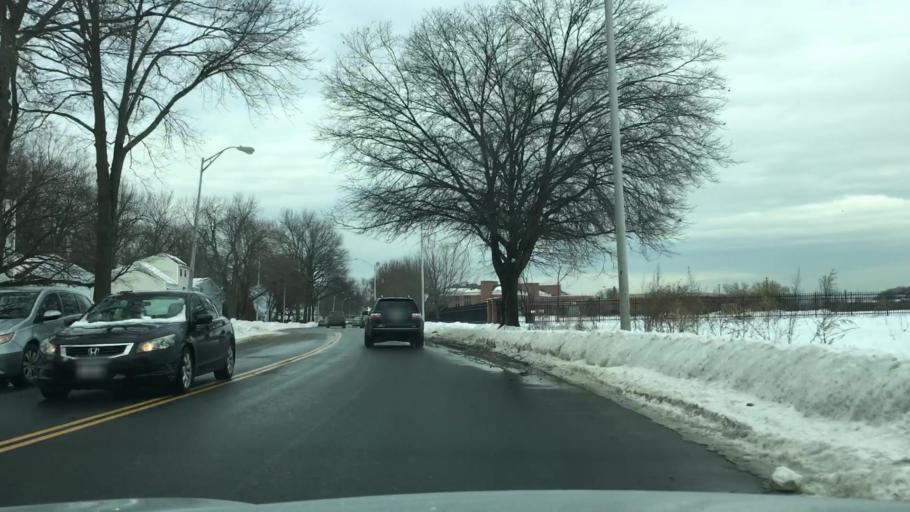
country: US
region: Massachusetts
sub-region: Hampden County
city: West Springfield
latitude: 42.1134
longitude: -72.6104
